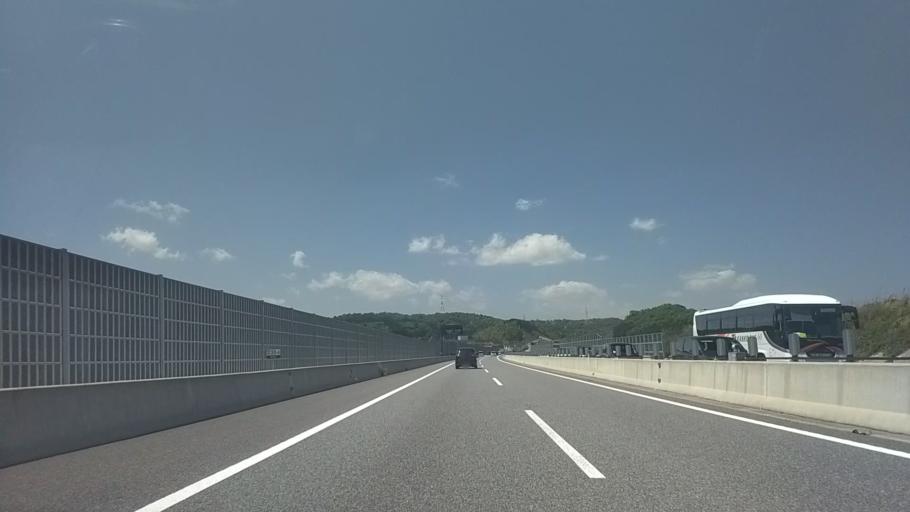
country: JP
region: Aichi
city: Gamagori
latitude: 34.9134
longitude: 137.2862
